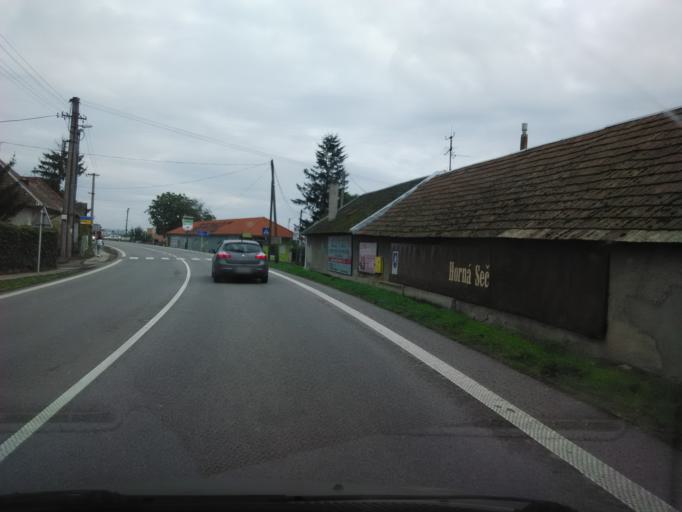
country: SK
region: Nitriansky
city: Levice
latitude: 48.1956
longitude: 18.5451
